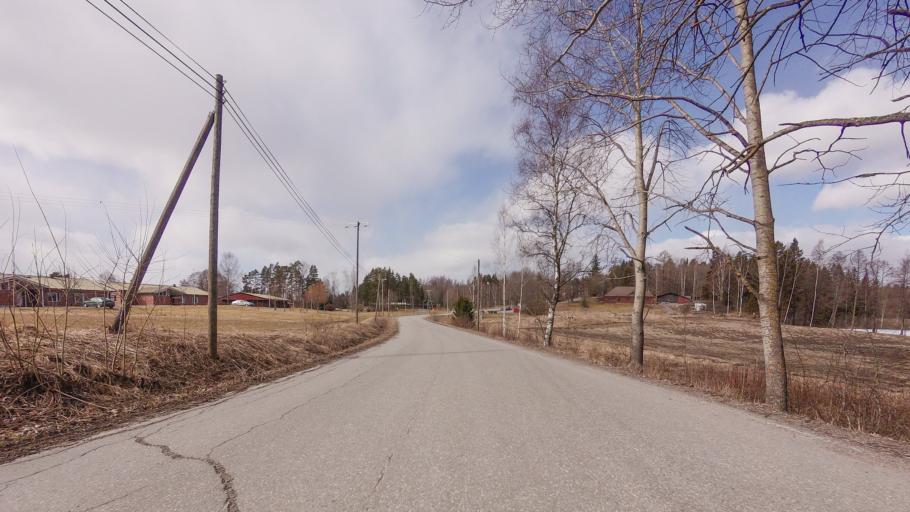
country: FI
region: Uusimaa
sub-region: Helsinki
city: Karjalohja
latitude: 60.2613
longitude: 23.7167
